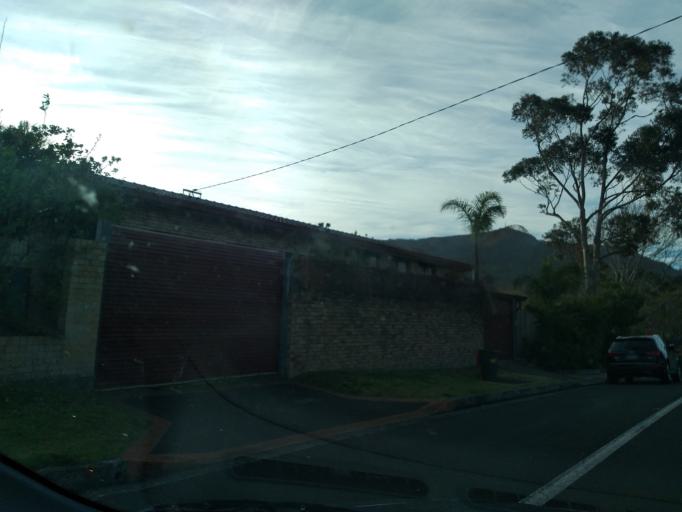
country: AU
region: New South Wales
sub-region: Wollongong
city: Mount Ousley
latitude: -34.3875
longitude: 150.8808
